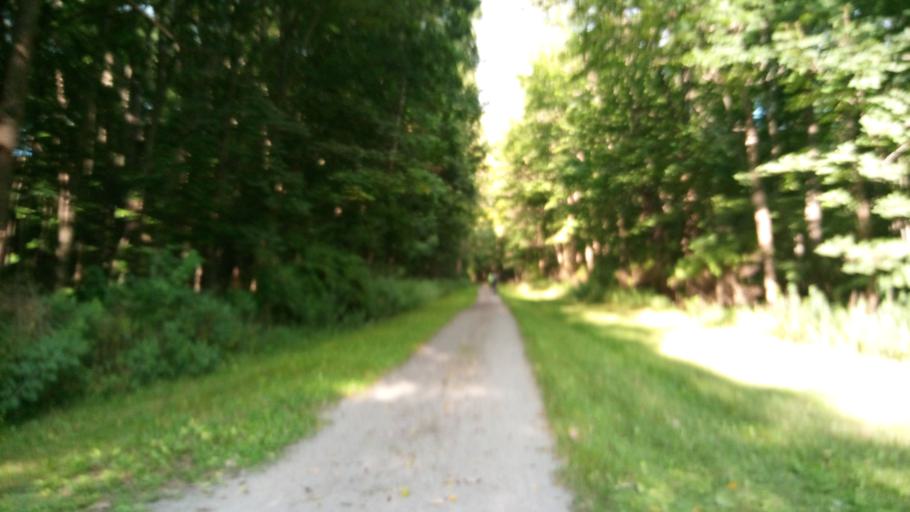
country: US
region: New York
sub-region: Monroe County
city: Honeoye Falls
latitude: 42.9930
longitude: -77.5204
